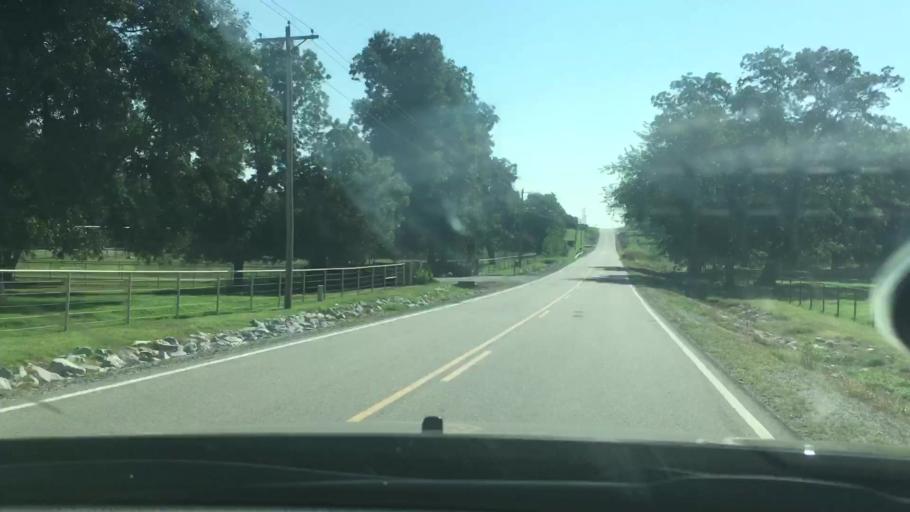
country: US
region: Oklahoma
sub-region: Love County
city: Marietta
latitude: 34.0275
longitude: -97.1659
